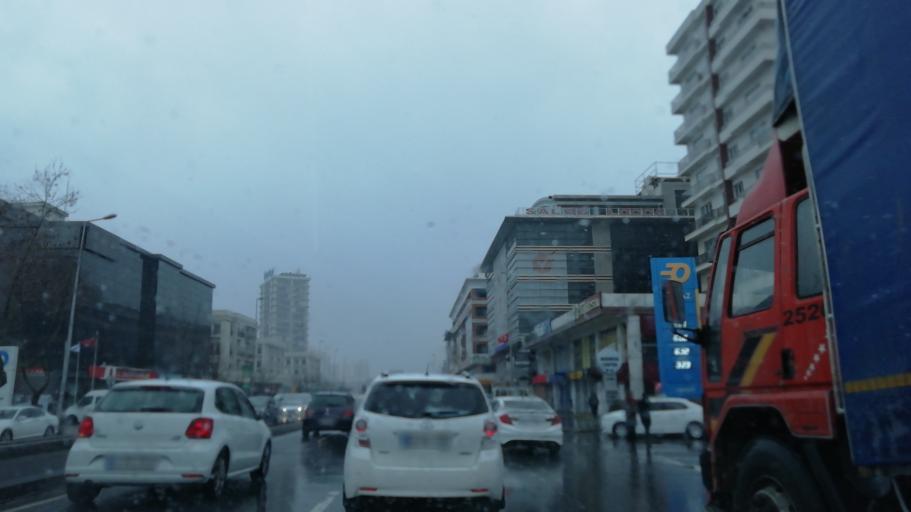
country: TR
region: Istanbul
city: Esenyurt
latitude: 41.0229
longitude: 28.6865
